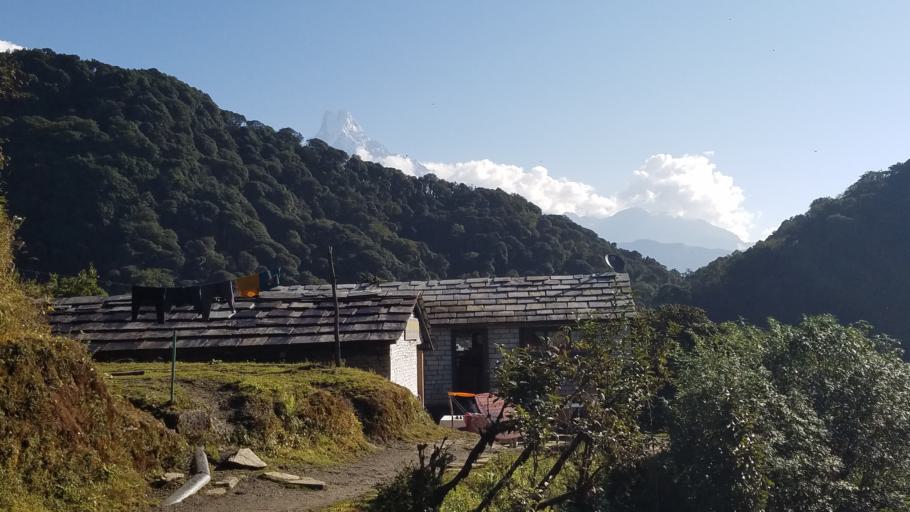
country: NP
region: Western Region
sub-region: Dhawalagiri Zone
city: Chitre
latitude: 28.3945
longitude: 83.7572
